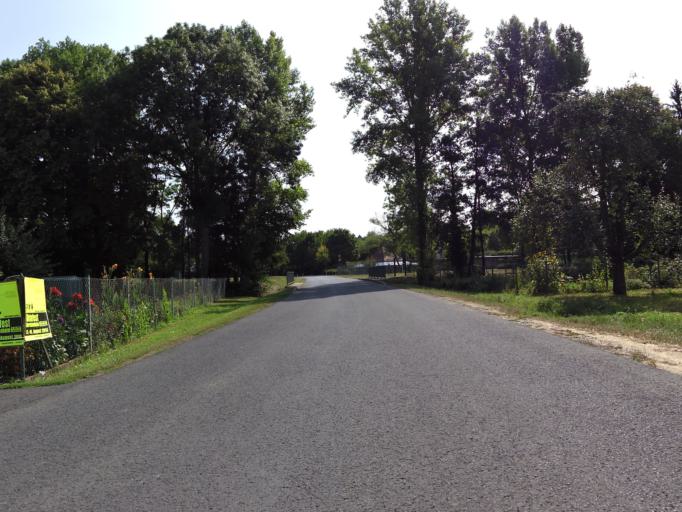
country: DE
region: Bavaria
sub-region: Regierungsbezirk Unterfranken
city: Estenfeld
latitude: 49.8335
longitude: 10.0116
